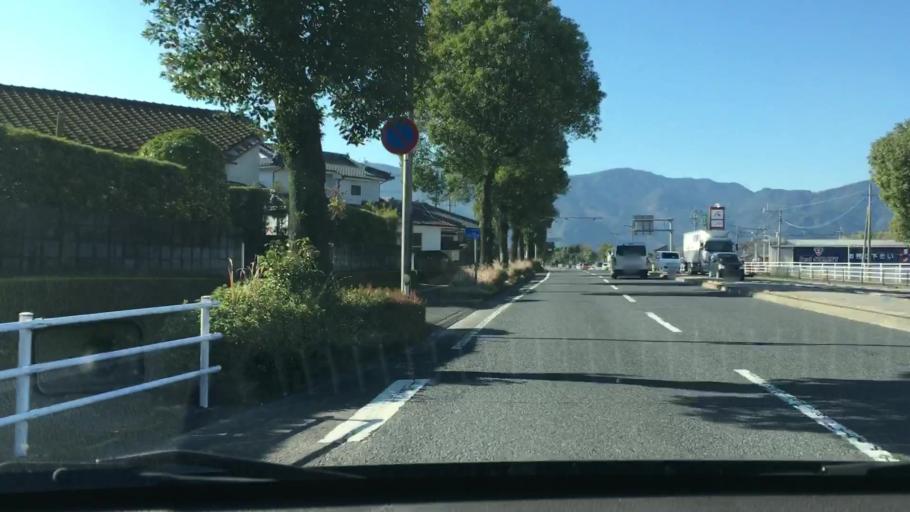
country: JP
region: Kagoshima
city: Kajiki
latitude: 31.7304
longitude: 130.6279
